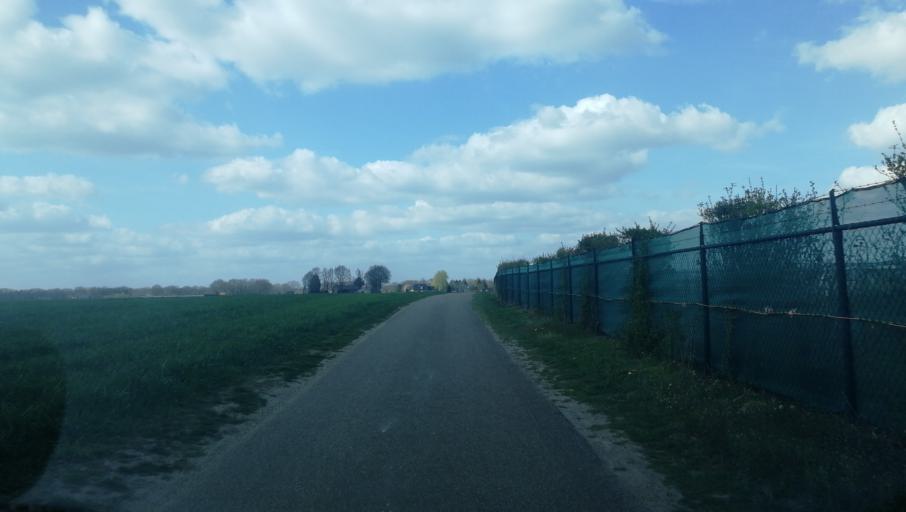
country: NL
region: Limburg
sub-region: Gemeente Peel en Maas
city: Maasbree
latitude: 51.3665
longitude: 6.0747
